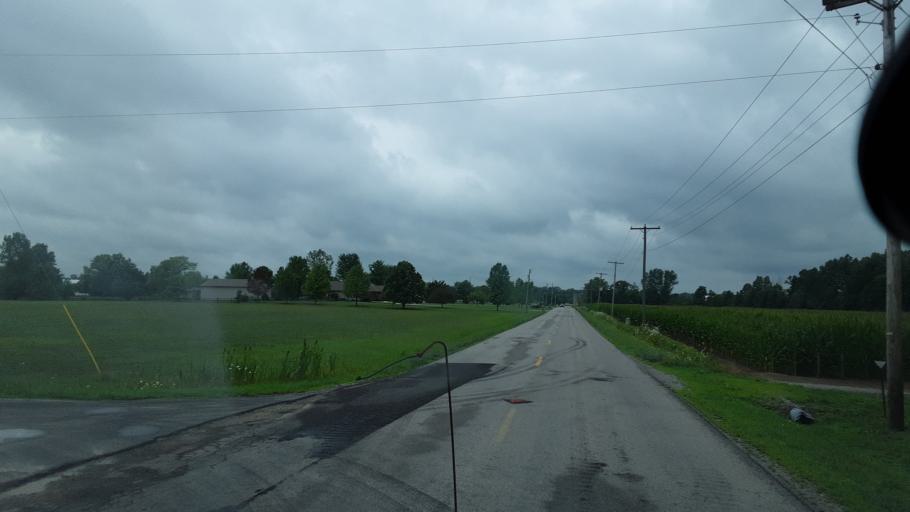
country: US
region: Indiana
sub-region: Allen County
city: New Haven
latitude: 40.9470
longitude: -85.0457
